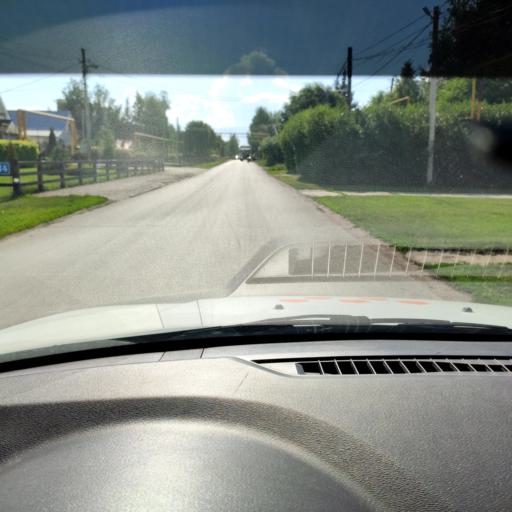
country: RU
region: Samara
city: Podstepki
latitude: 53.5112
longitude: 49.1442
